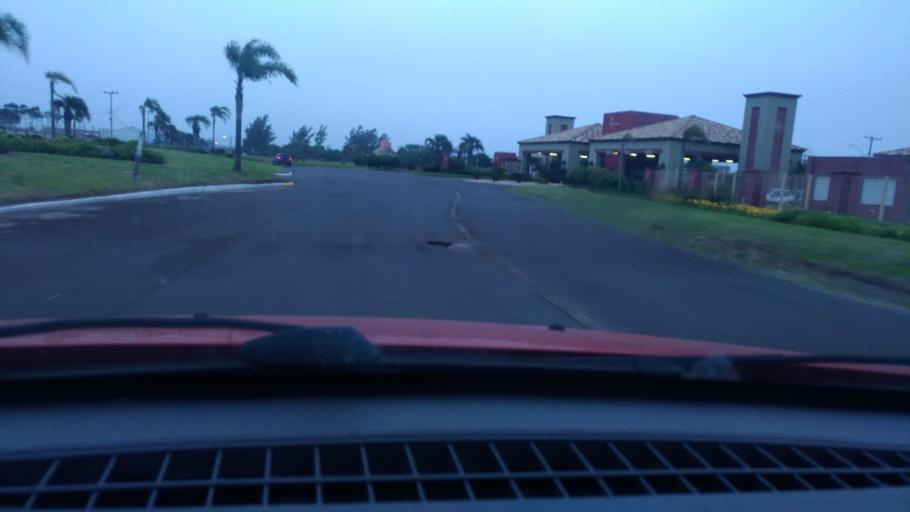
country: BR
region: Rio Grande do Sul
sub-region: Capao Da Canoa
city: Capao da Canoa
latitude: -29.8493
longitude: -50.0762
